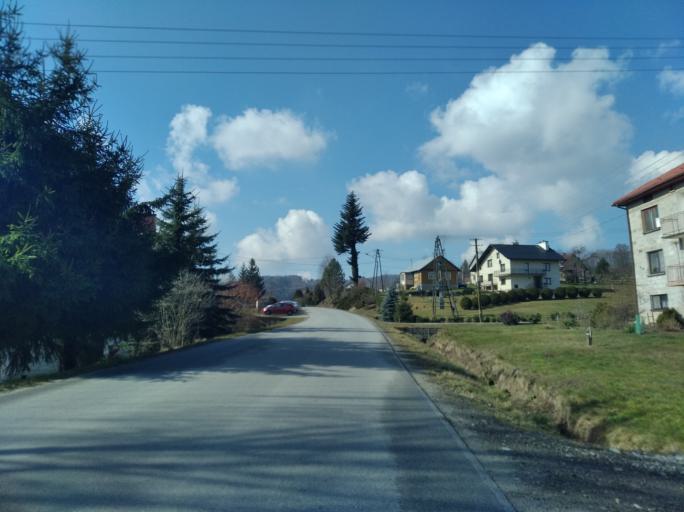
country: PL
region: Subcarpathian Voivodeship
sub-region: Powiat strzyzowski
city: Frysztak
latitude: 49.8734
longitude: 21.5742
